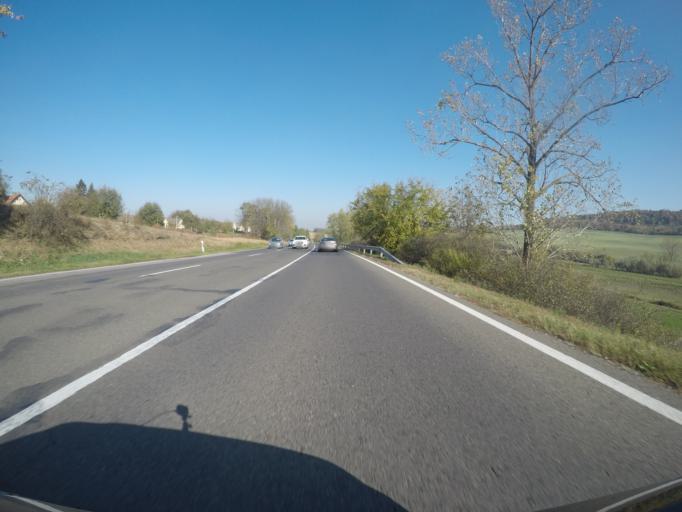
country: HU
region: Tolna
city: Bonyhad
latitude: 46.3311
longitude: 18.5803
